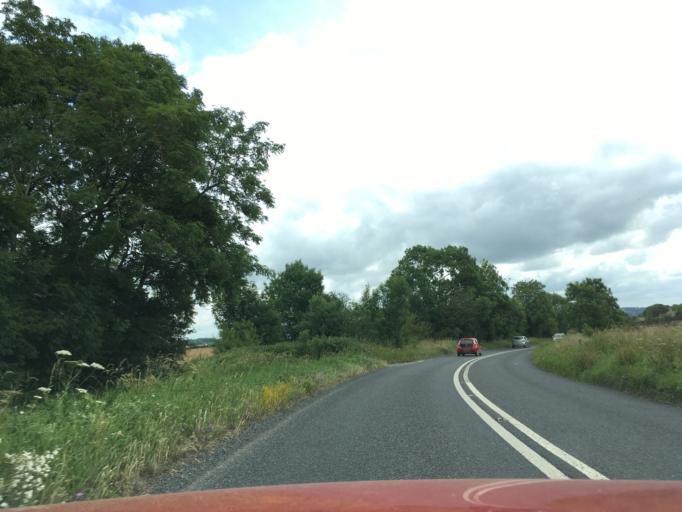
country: GB
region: England
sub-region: Gloucestershire
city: Westfield
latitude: 51.8893
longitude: -1.8120
